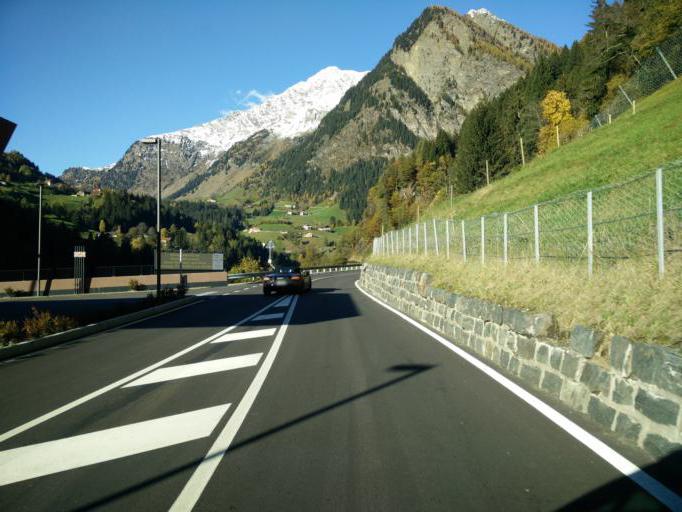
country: IT
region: Trentino-Alto Adige
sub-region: Bolzano
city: Moso in Passiria
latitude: 46.8272
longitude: 11.1784
